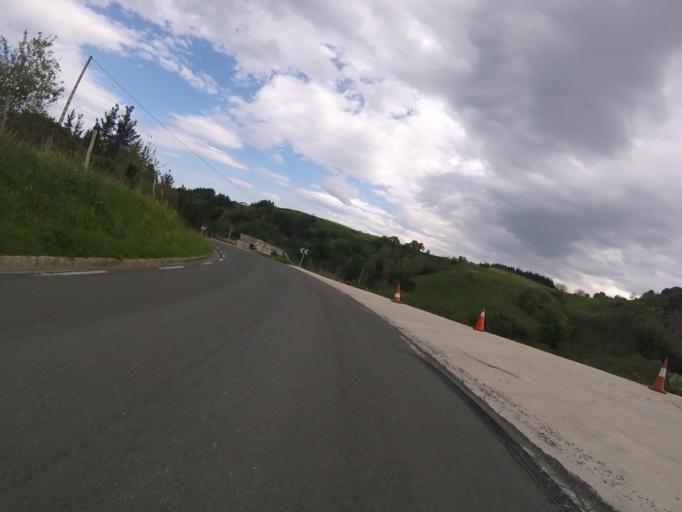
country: ES
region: Basque Country
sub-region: Provincia de Guipuzcoa
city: Zarautz
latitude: 43.2694
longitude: -2.1663
